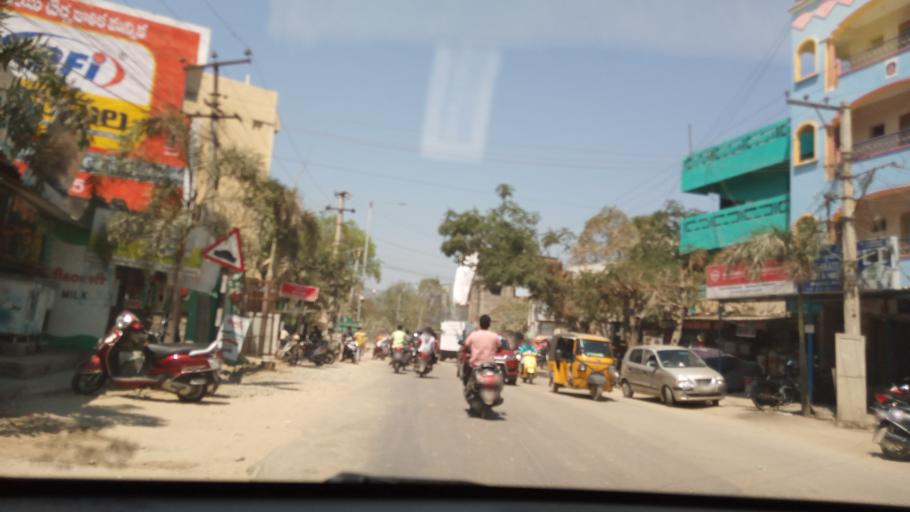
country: IN
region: Andhra Pradesh
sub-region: Chittoor
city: Tirupati
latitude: 13.6150
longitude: 79.4167
